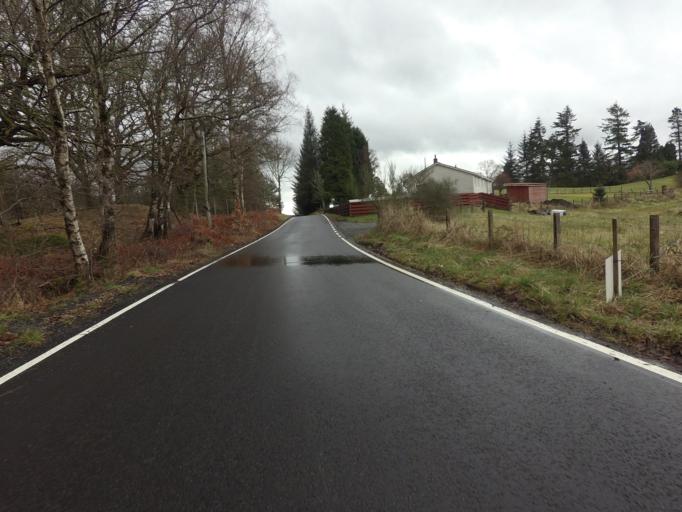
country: GB
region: Scotland
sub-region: Stirling
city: Killearn
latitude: 56.1914
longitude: -4.5055
